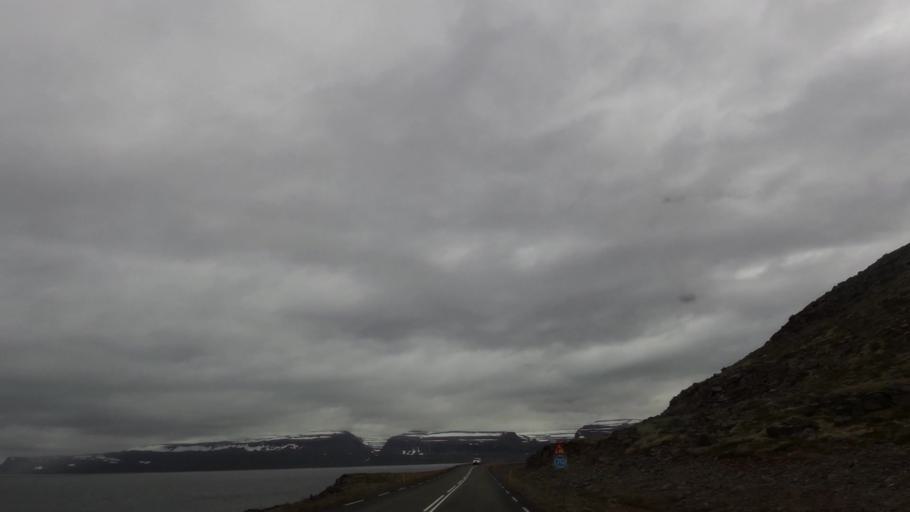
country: IS
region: Westfjords
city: Isafjoerdur
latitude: 66.0518
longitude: -22.7664
